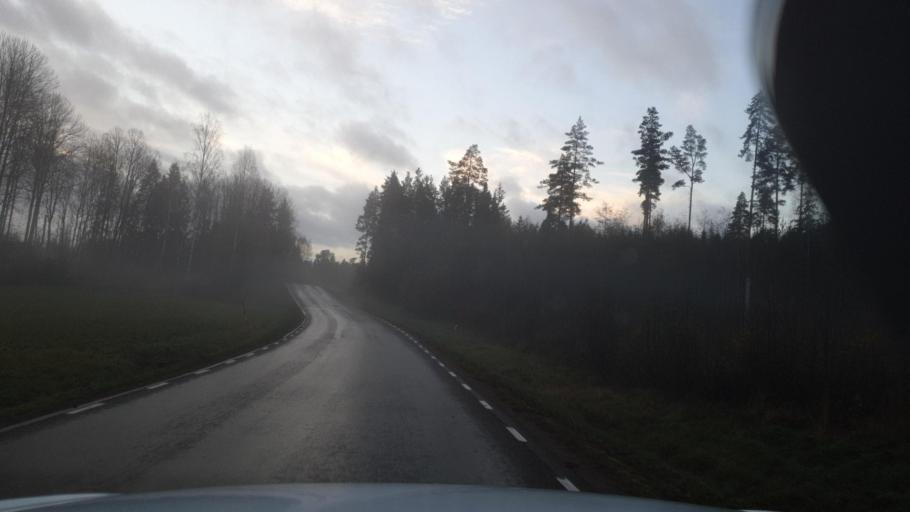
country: SE
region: Vaermland
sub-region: Arvika Kommun
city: Arvika
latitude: 59.6324
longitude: 12.7972
